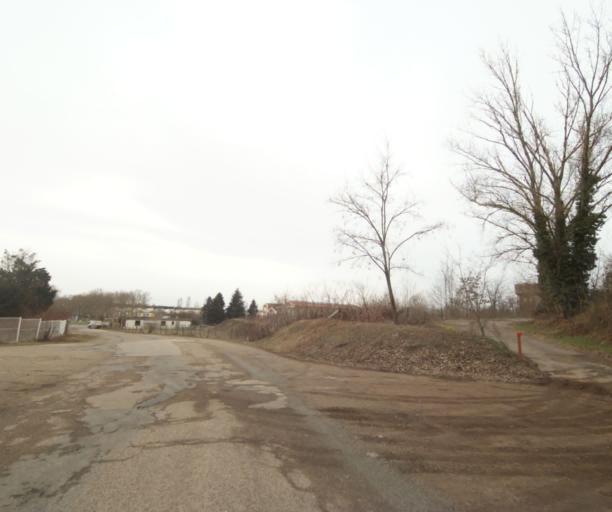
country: FR
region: Rhone-Alpes
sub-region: Departement de la Loire
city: Mably
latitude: 46.0661
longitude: 4.0933
